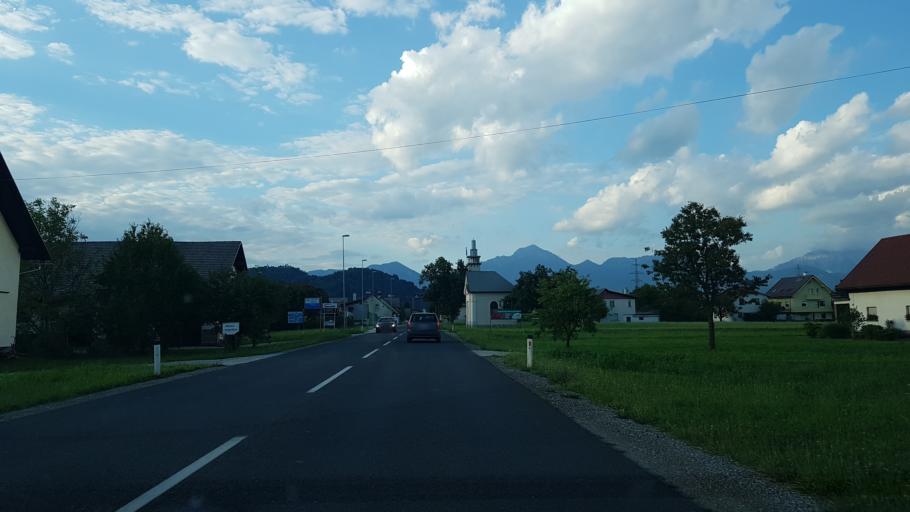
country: SI
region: Kranj
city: Zgornje Bitnje
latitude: 46.2137
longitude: 14.3377
